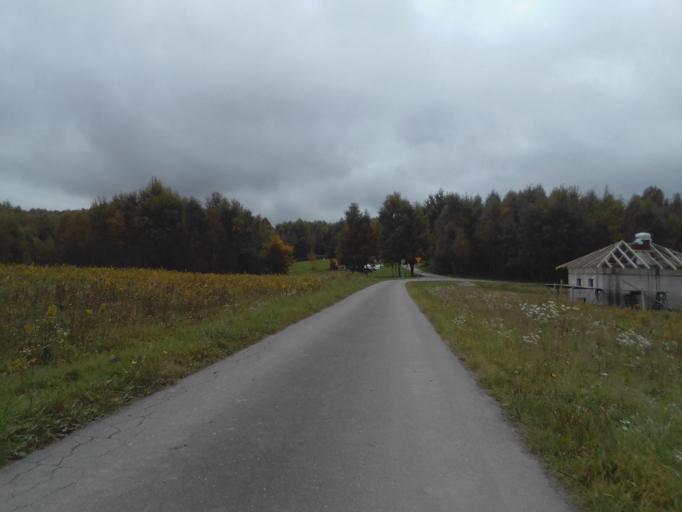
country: PL
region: Subcarpathian Voivodeship
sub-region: Powiat strzyzowski
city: Gwoznica Gorna
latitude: 49.8377
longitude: 22.0071
